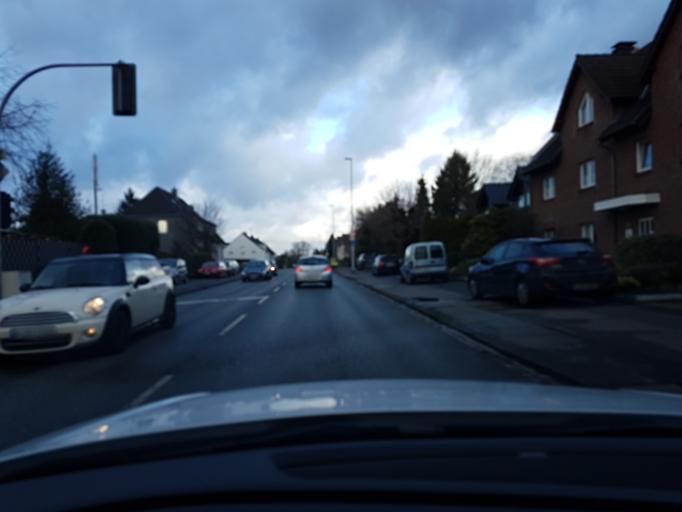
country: DE
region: North Rhine-Westphalia
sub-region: Regierungsbezirk Dusseldorf
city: Muelheim (Ruhr)
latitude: 51.3686
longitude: 6.8634
